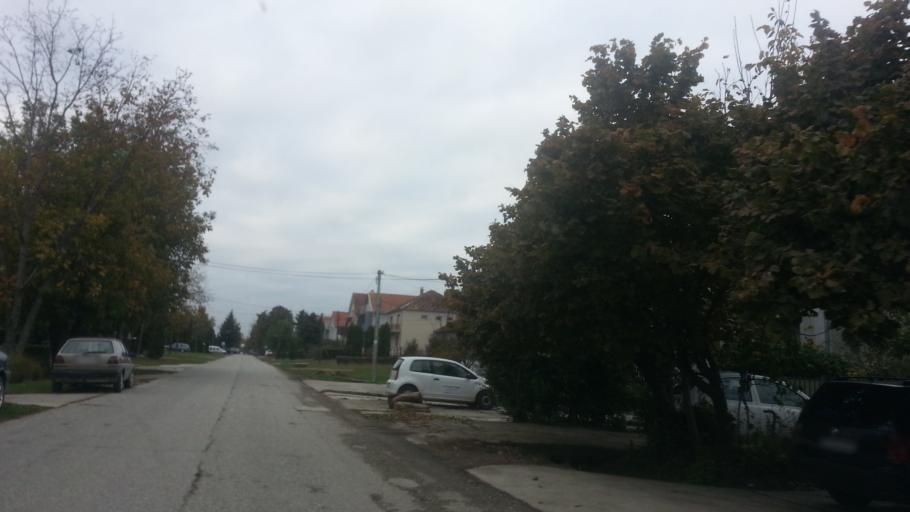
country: RS
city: Novi Banovci
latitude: 44.9456
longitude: 20.2890
